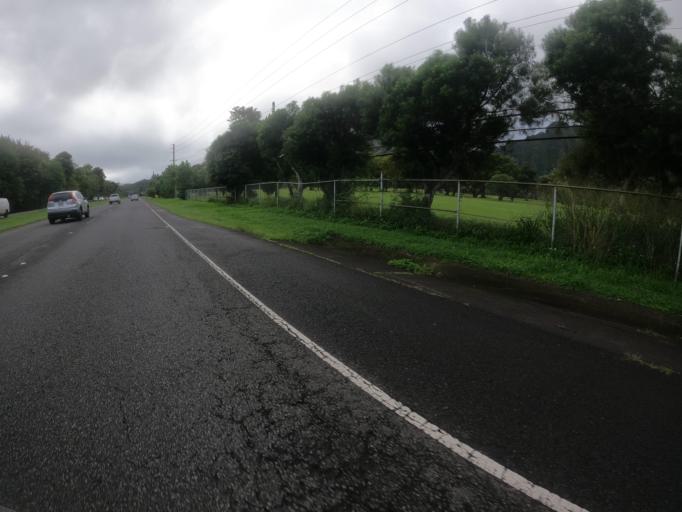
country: US
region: Hawaii
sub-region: Honolulu County
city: Maunawili
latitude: 21.3820
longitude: -157.7879
